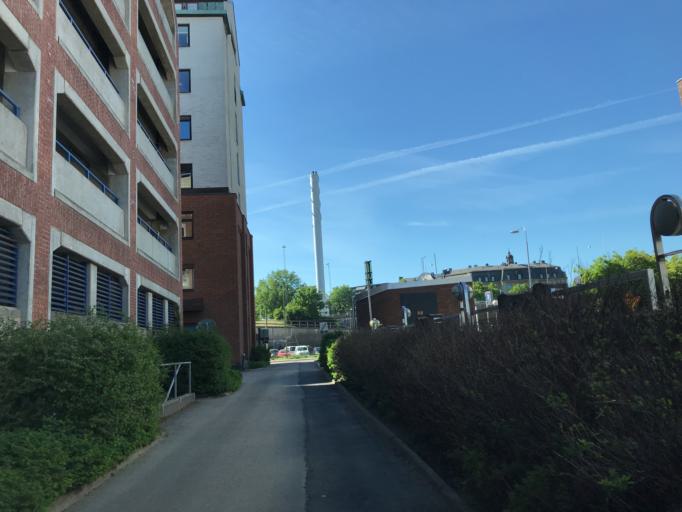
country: SE
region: Stockholm
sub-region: Stockholms Kommun
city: Arsta
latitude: 59.3110
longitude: 18.0311
